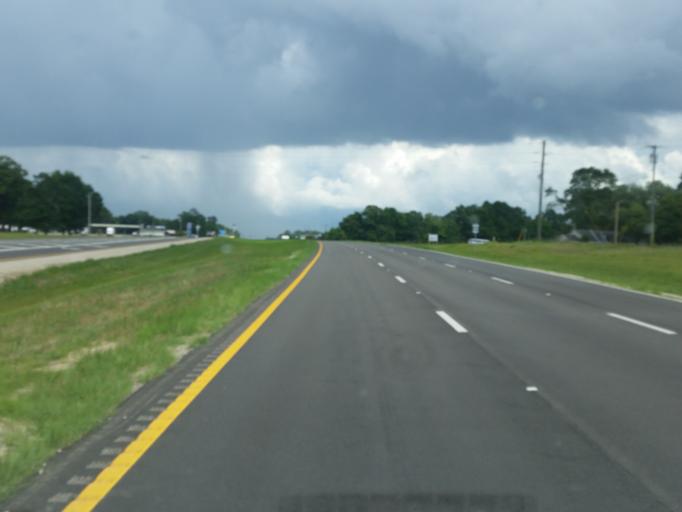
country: US
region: Mississippi
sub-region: George County
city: Lucedale
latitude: 30.9252
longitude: -88.5140
